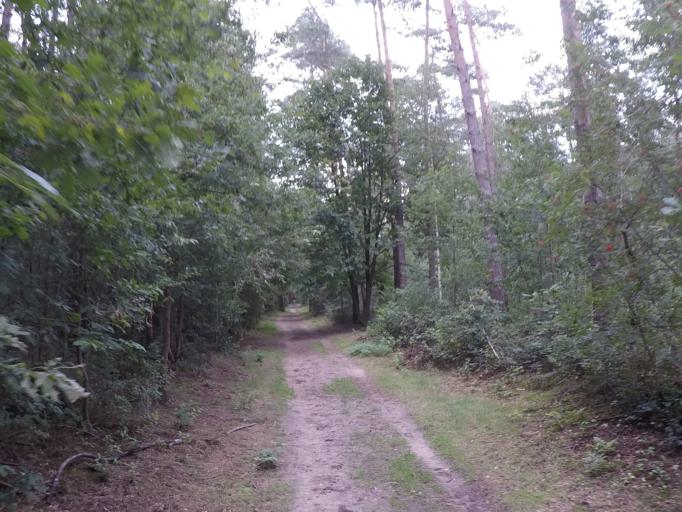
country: BE
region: Flanders
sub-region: Provincie Antwerpen
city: Grobbendonk
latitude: 51.2042
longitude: 4.7499
